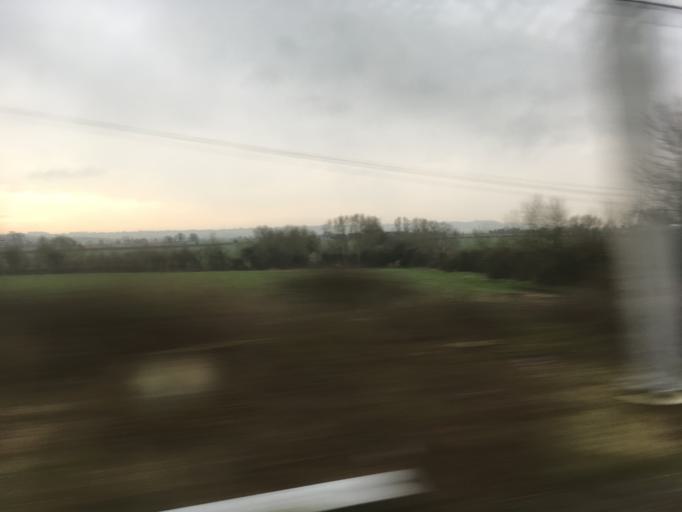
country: GB
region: England
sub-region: Wiltshire
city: Lyneham
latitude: 51.5564
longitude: -1.9861
